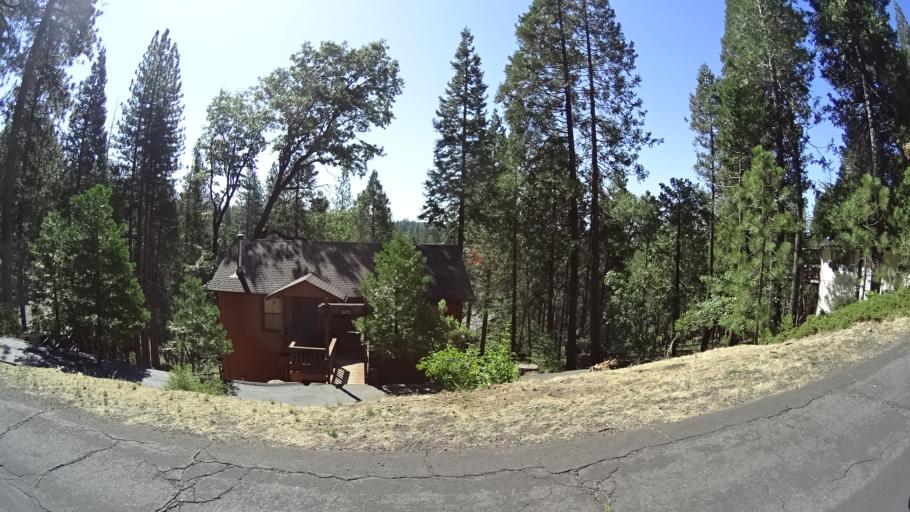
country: US
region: California
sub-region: Calaveras County
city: Arnold
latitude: 38.2437
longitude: -120.3681
